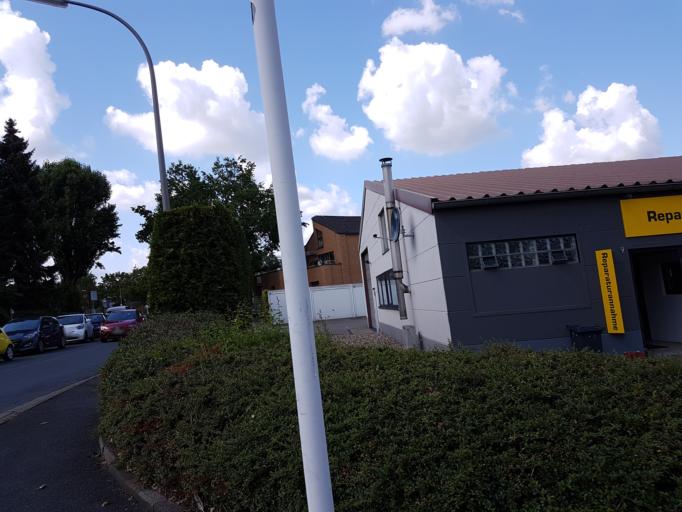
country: DE
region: North Rhine-Westphalia
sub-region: Regierungsbezirk Arnsberg
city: Holzwickede
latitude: 51.5318
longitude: 7.6262
